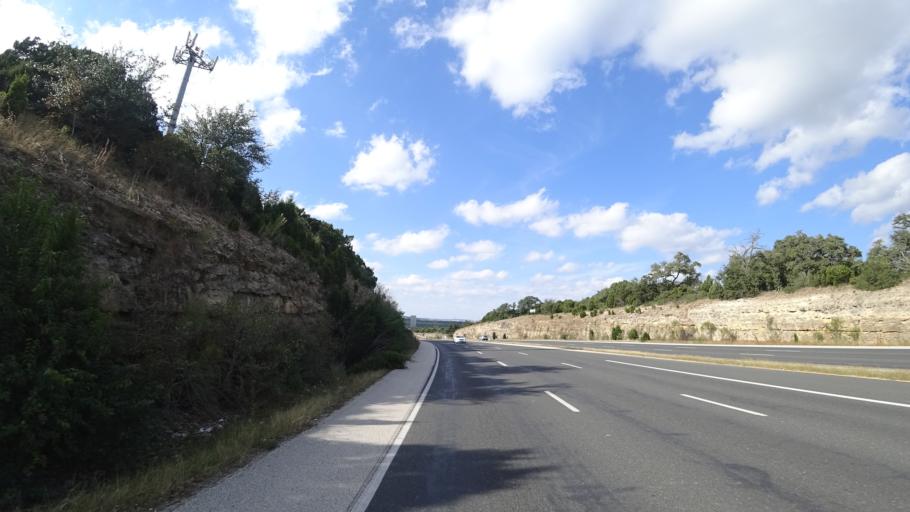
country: US
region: Texas
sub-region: Travis County
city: Barton Creek
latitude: 30.2608
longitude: -97.8849
